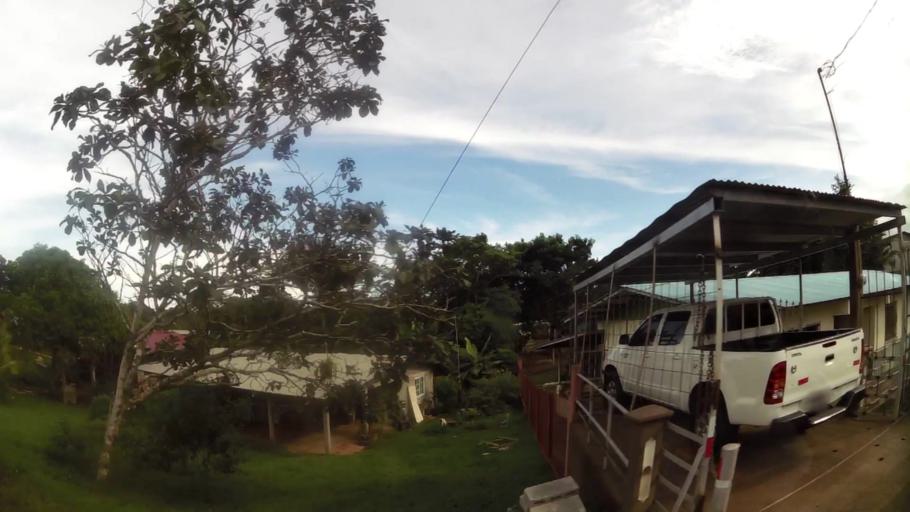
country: PA
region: Panama
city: El Coco
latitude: 8.8773
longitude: -79.8061
